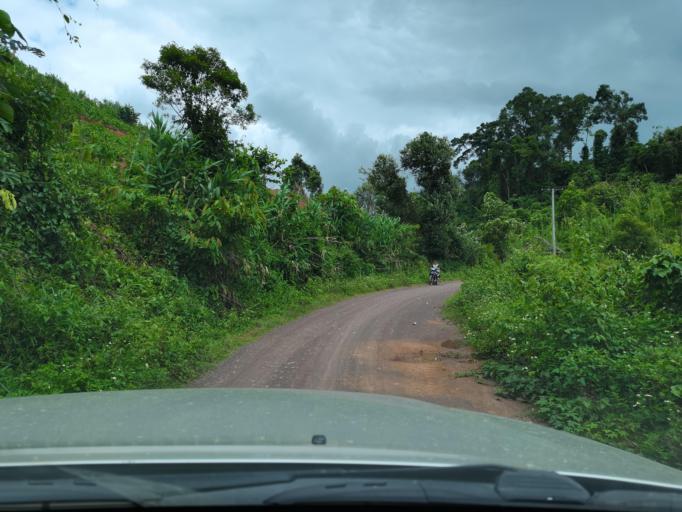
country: LA
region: Loungnamtha
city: Muang Long
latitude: 20.7045
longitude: 101.0122
